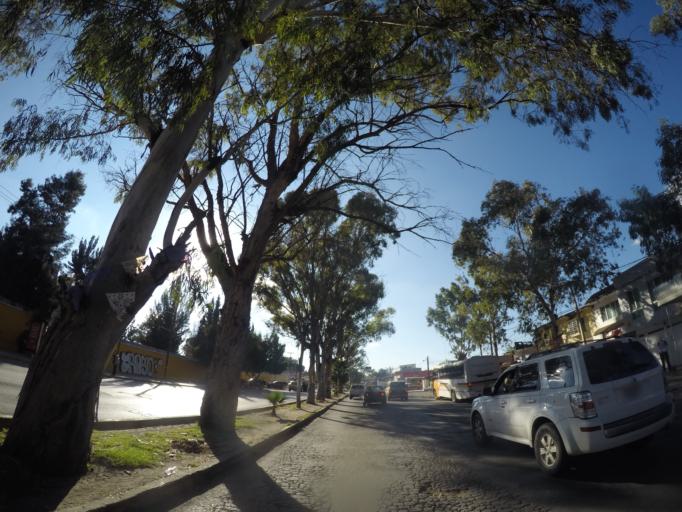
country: MX
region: San Luis Potosi
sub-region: San Luis Potosi
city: San Luis Potosi
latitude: 22.1829
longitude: -101.0003
